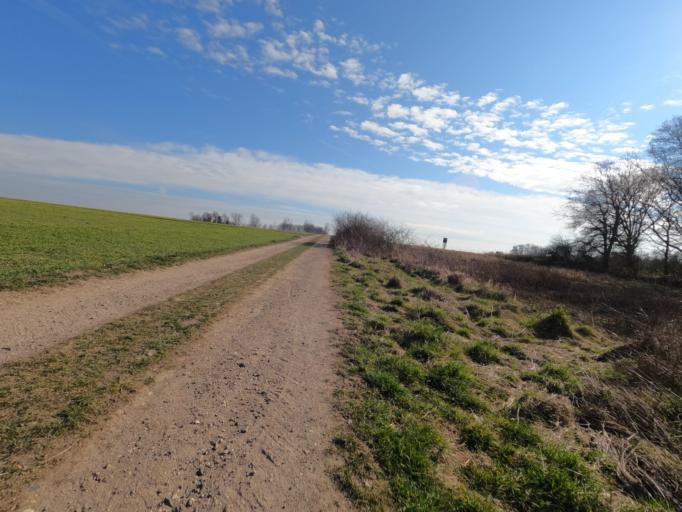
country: DE
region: North Rhine-Westphalia
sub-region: Regierungsbezirk Koln
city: Linnich
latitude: 51.0271
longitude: 6.2873
